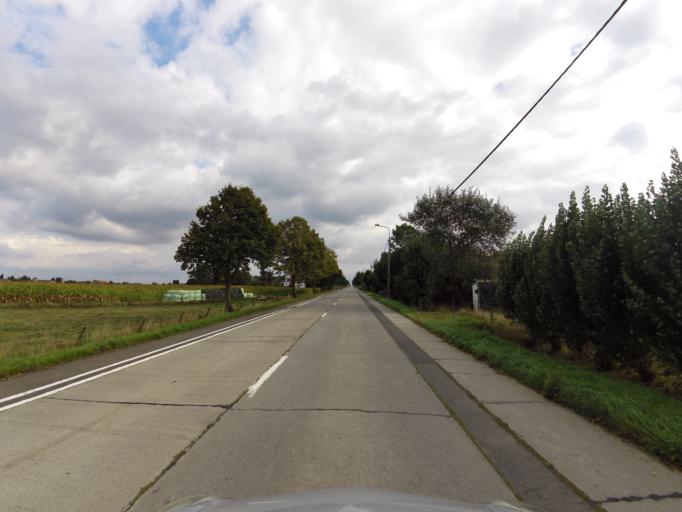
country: BE
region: Flanders
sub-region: Provincie West-Vlaanderen
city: Tielt
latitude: 51.0039
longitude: 3.2995
